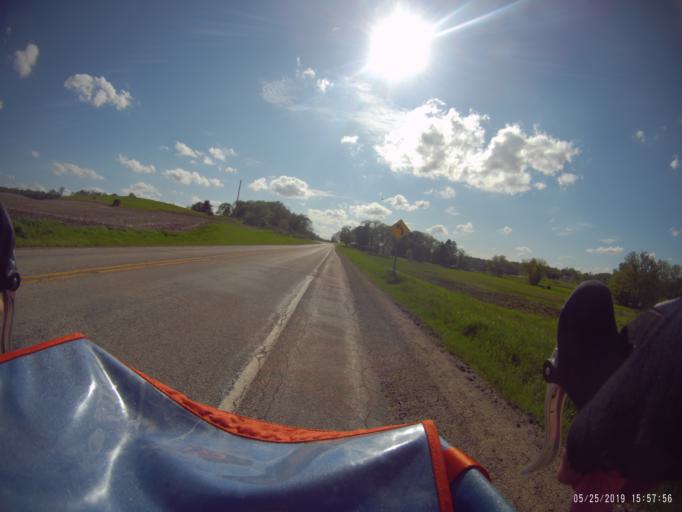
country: US
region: Wisconsin
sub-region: Dane County
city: Verona
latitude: 42.9697
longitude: -89.6090
